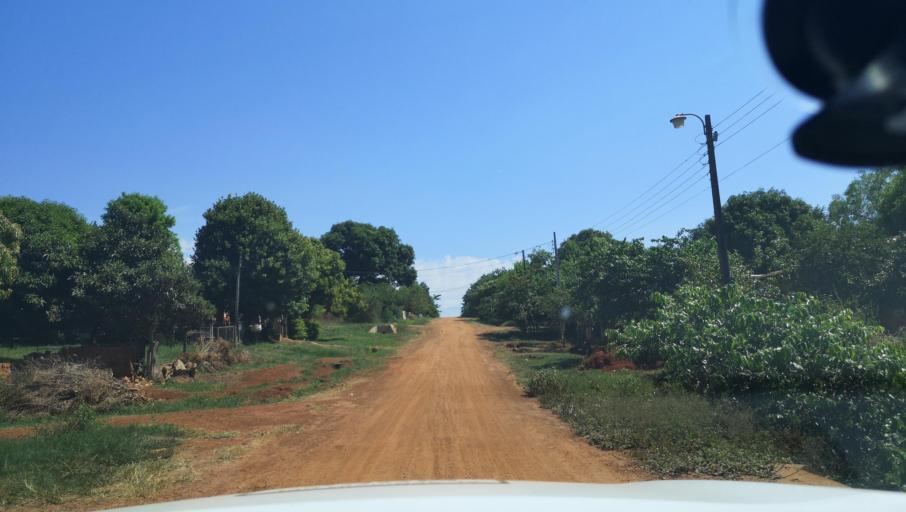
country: PY
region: Itapua
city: Carmen del Parana
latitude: -27.1668
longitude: -56.2478
